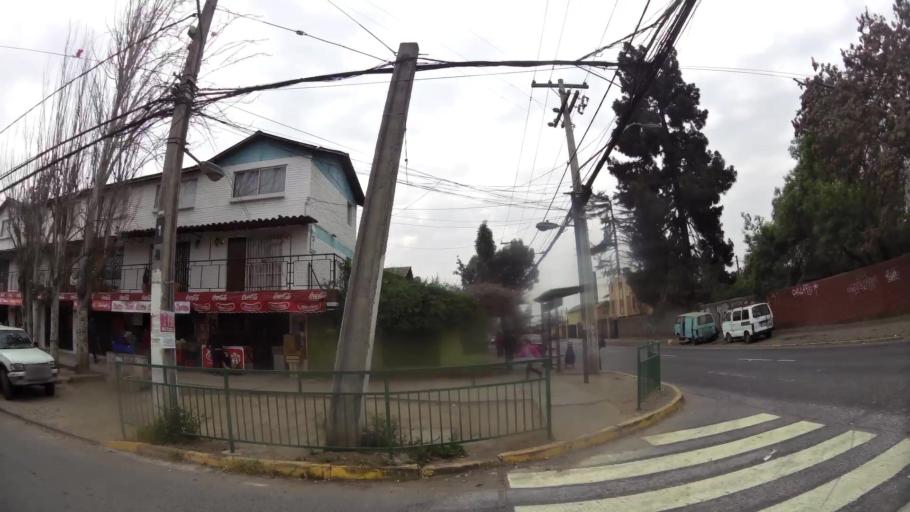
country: CL
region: Santiago Metropolitan
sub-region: Provincia de Santiago
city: Villa Presidente Frei, Nunoa, Santiago, Chile
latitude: -33.4963
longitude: -70.5887
